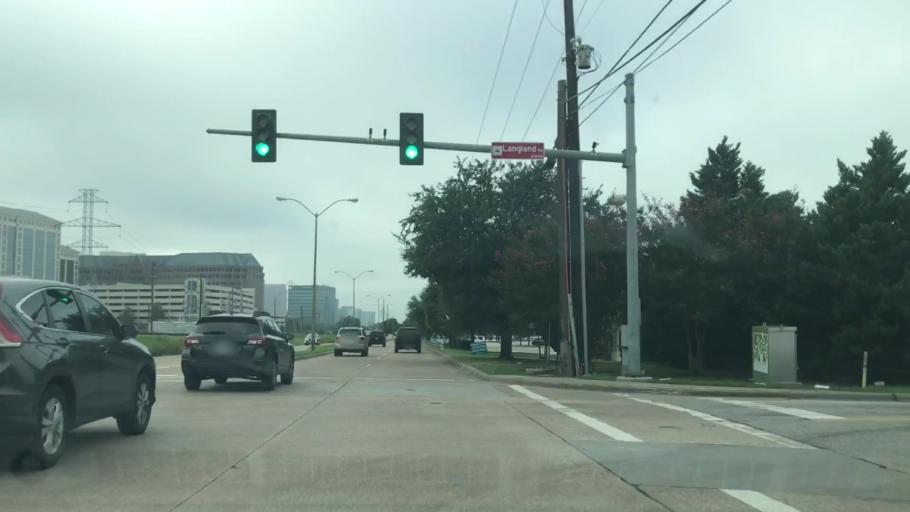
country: US
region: Texas
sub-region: Dallas County
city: Addison
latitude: 32.9451
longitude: -96.8275
